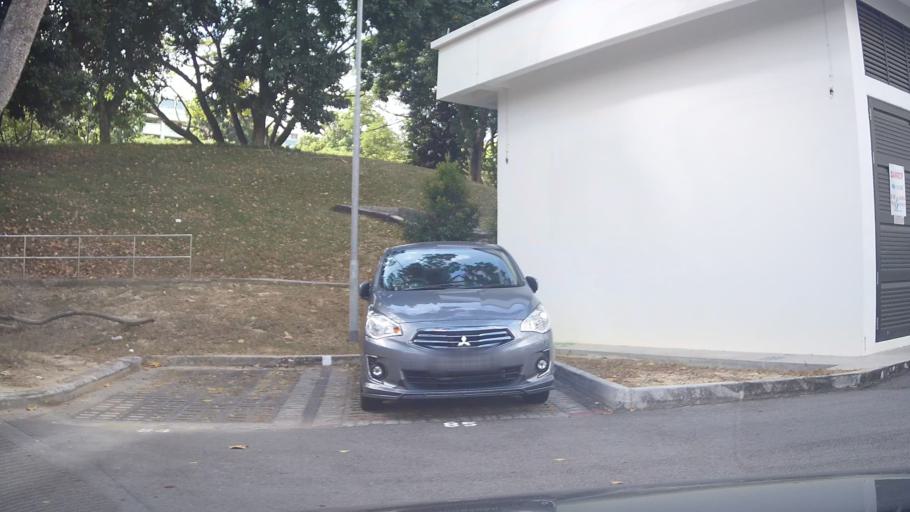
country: SG
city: Singapore
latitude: 1.3475
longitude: 103.9530
